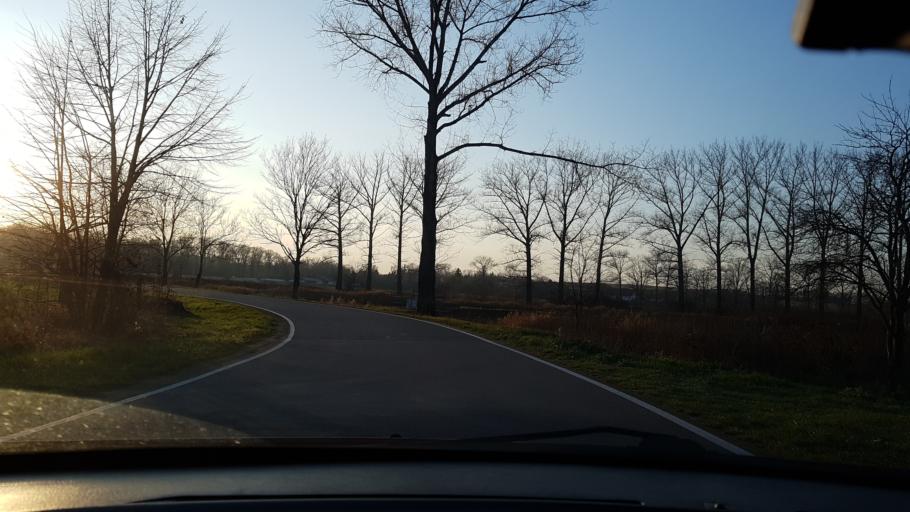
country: PL
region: Lower Silesian Voivodeship
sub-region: Powiat zabkowicki
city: Henrykow
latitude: 50.6590
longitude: 17.0237
